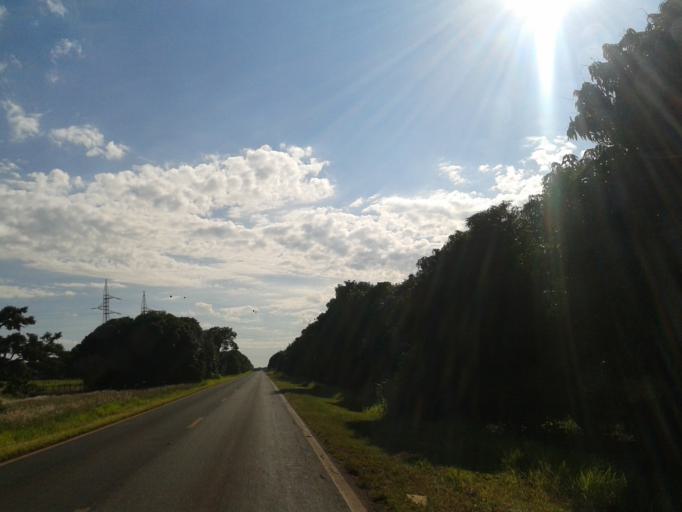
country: BR
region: Minas Gerais
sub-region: Centralina
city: Centralina
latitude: -18.7260
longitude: -49.1836
